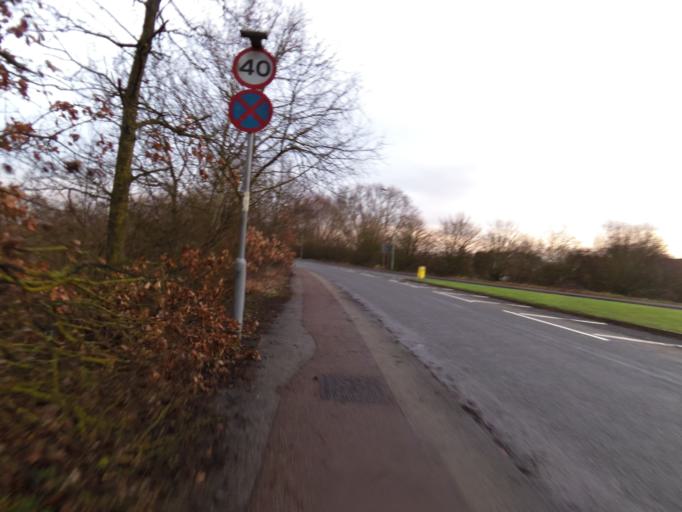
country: GB
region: England
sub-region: Suffolk
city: Stowmarket
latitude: 52.1800
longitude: 1.0052
